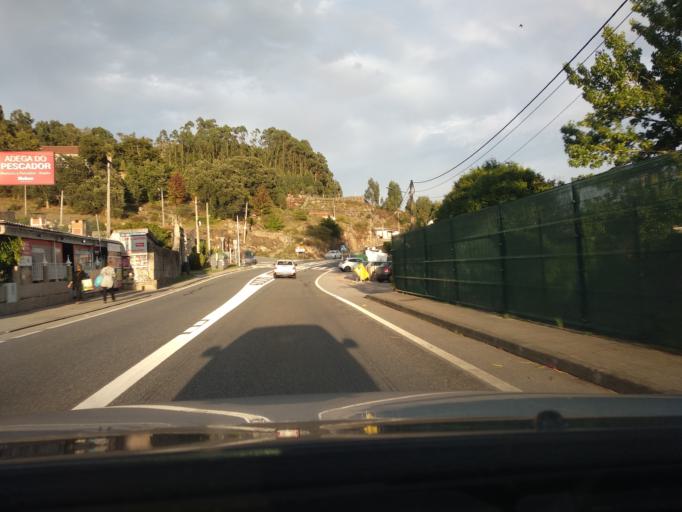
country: ES
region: Galicia
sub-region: Provincia de Pontevedra
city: Redondela
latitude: 42.2916
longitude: -8.6749
